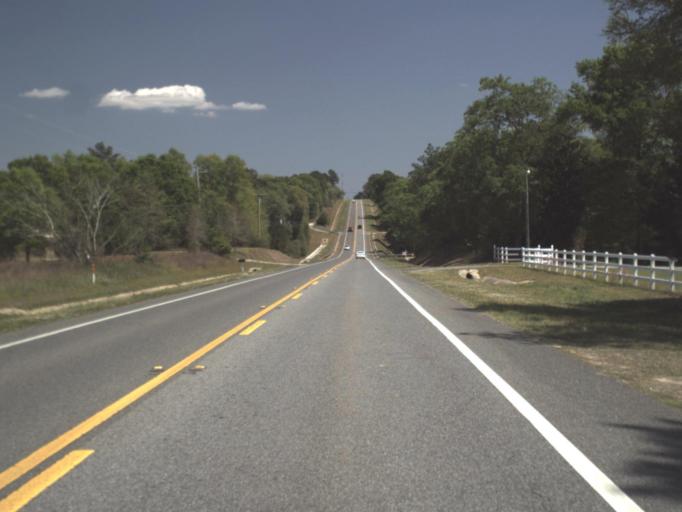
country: US
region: Florida
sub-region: Escambia County
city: Century
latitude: 30.9488
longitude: -87.1895
